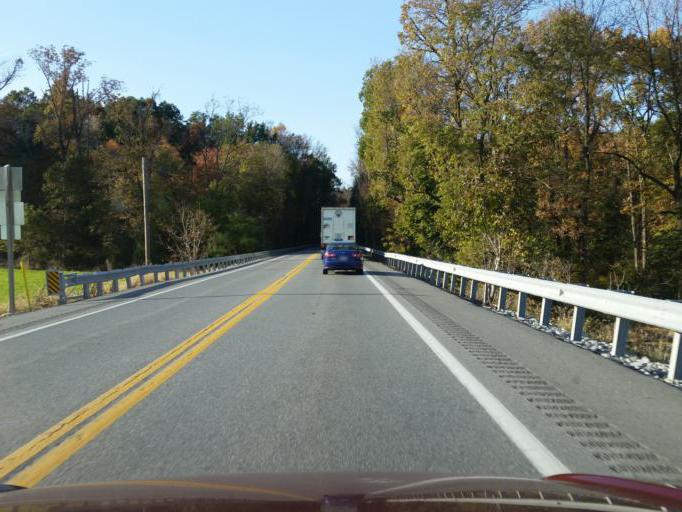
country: US
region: Pennsylvania
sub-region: Lancaster County
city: Elizabethtown
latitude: 40.2140
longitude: -76.6162
